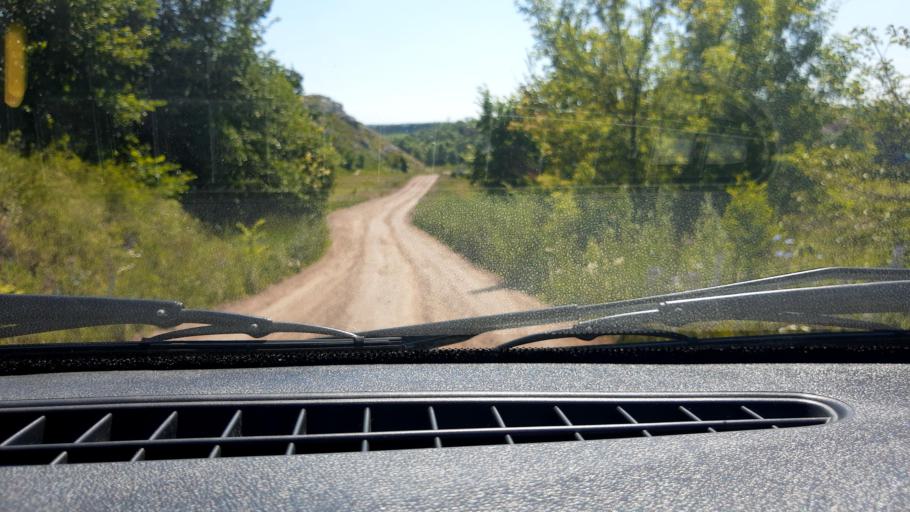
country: RU
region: Bashkortostan
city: Karmaskaly
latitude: 54.3608
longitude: 55.8961
